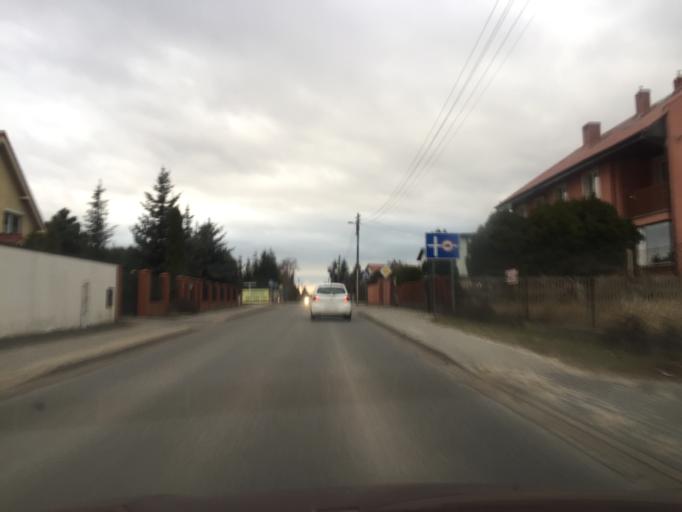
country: PL
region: Greater Poland Voivodeship
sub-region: Powiat poznanski
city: Plewiska
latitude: 52.3656
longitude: 16.8262
